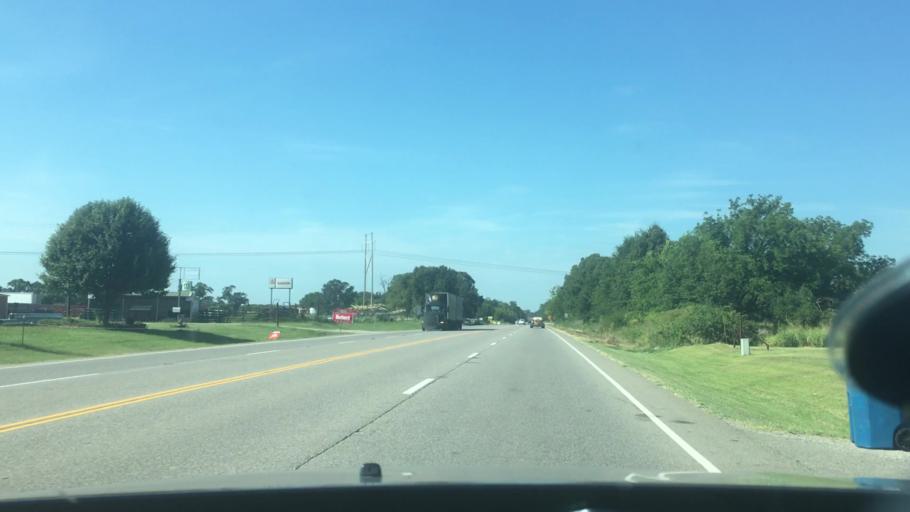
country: US
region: Oklahoma
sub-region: Atoka County
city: Atoka
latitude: 34.3402
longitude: -96.1547
